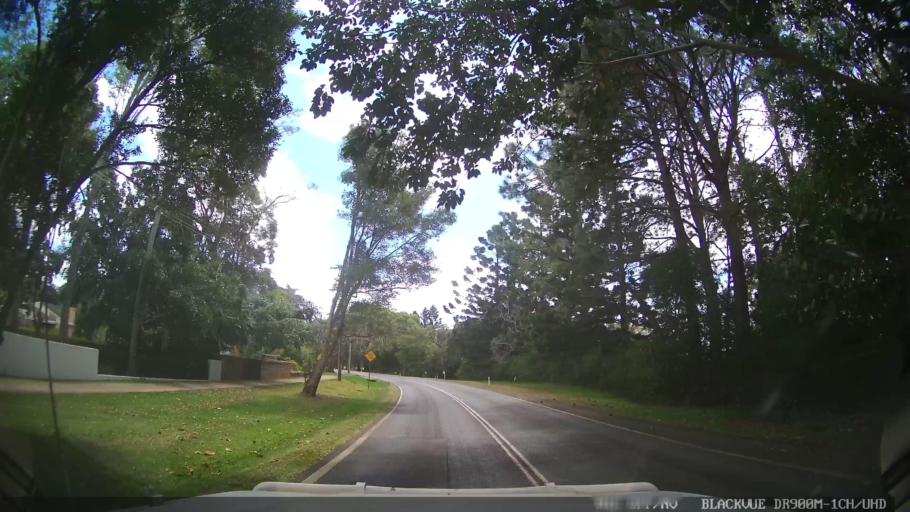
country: AU
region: Queensland
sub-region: Sunshine Coast
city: Nambour
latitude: -26.6611
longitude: 152.8832
